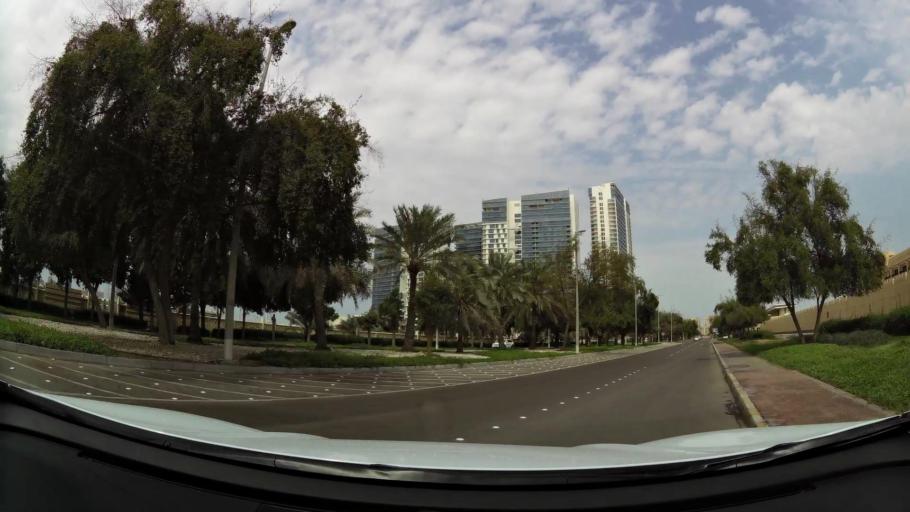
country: AE
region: Abu Dhabi
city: Abu Dhabi
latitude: 24.4107
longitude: 54.4633
